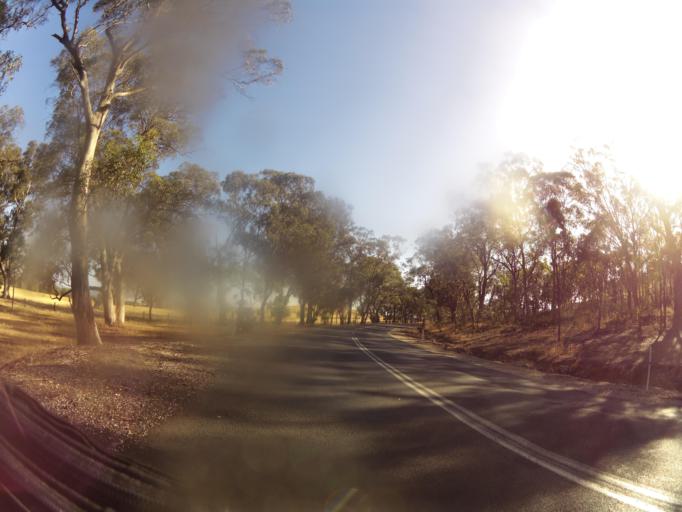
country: AU
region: Victoria
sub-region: Murrindindi
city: Kinglake West
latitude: -37.0082
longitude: 145.1242
